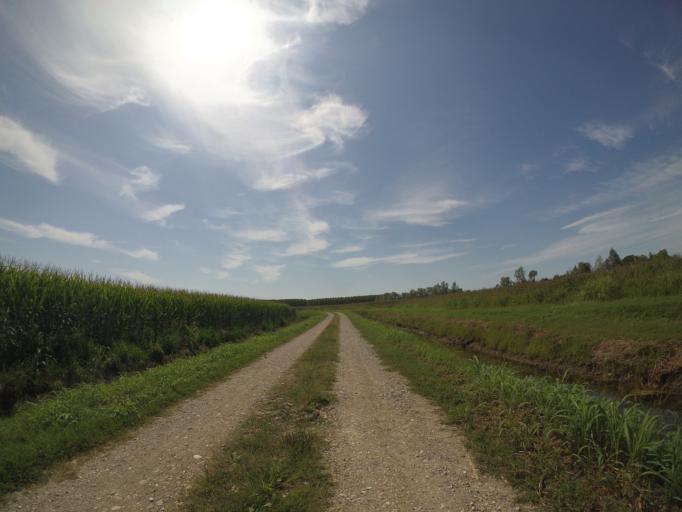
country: IT
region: Friuli Venezia Giulia
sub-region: Provincia di Udine
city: Varmo
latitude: 45.9214
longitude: 13.0141
